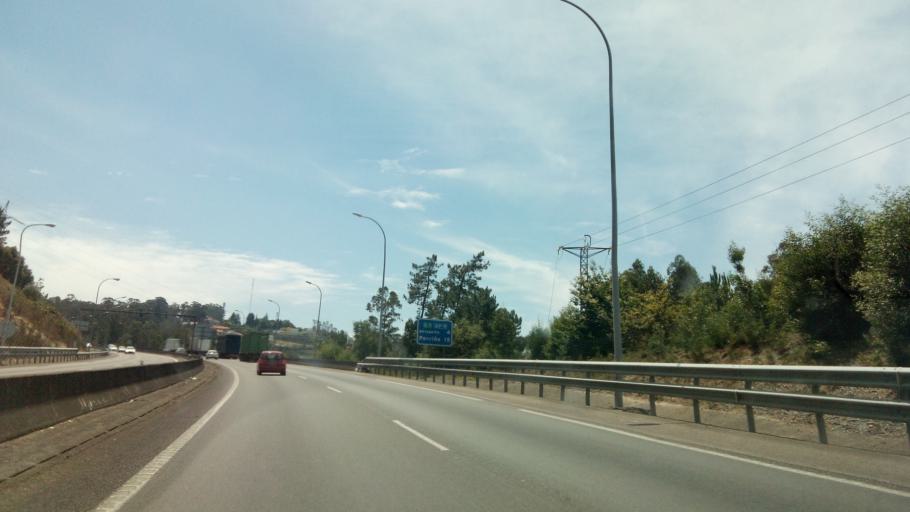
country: ES
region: Galicia
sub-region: Provincia de Pontevedra
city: Vigo
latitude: 42.2494
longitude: -8.6813
